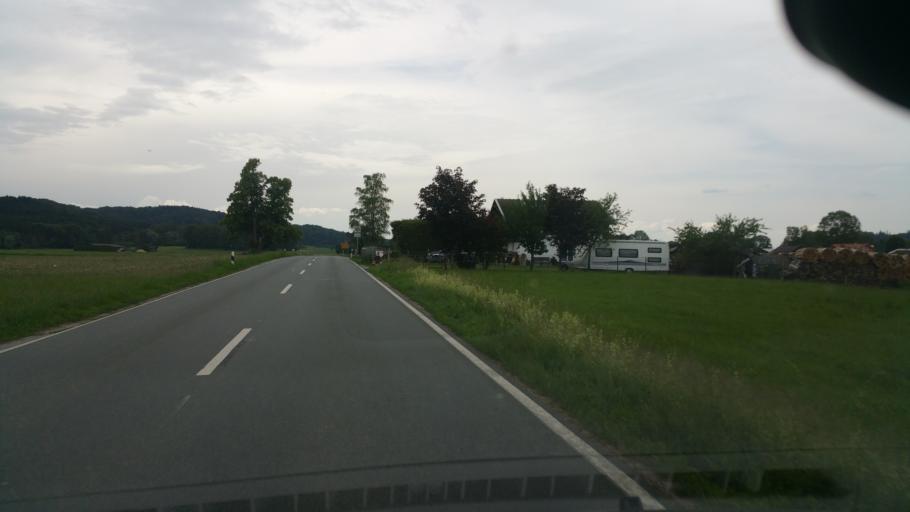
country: DE
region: Bavaria
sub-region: Upper Bavaria
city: Bruckmuhl
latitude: 47.8662
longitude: 11.9257
